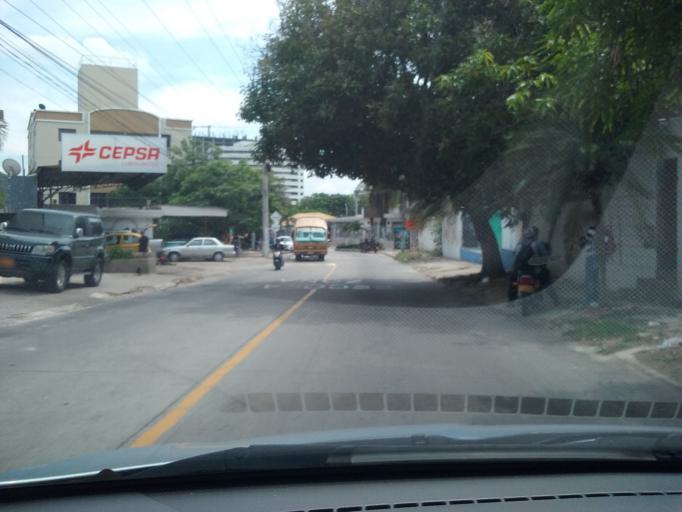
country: CO
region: Atlantico
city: Barranquilla
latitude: 11.0099
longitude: -74.8057
